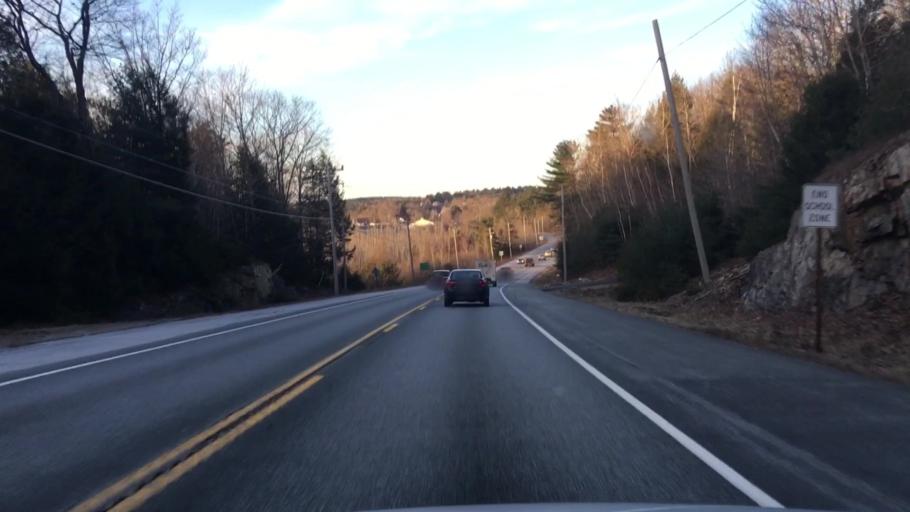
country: US
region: Maine
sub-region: Hancock County
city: Dedham
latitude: 44.7292
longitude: -68.6236
